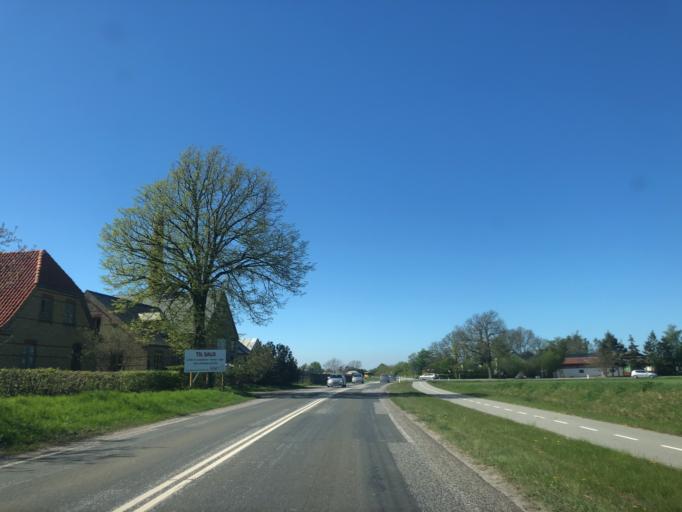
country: DK
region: Zealand
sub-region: Stevns Kommune
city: Stroby Egede
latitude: 55.3744
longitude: 12.2947
